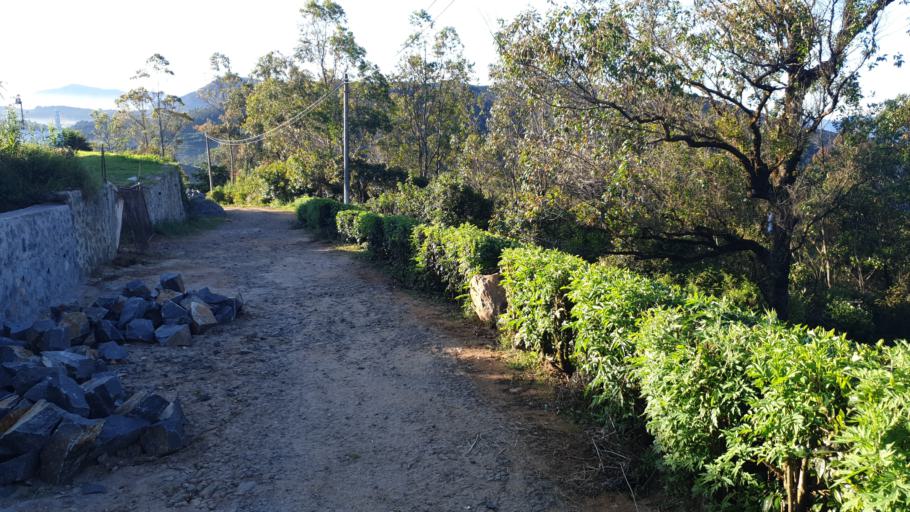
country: LK
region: Central
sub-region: Nuwara Eliya District
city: Nuwara Eliya
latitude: 6.9549
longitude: 80.7661
